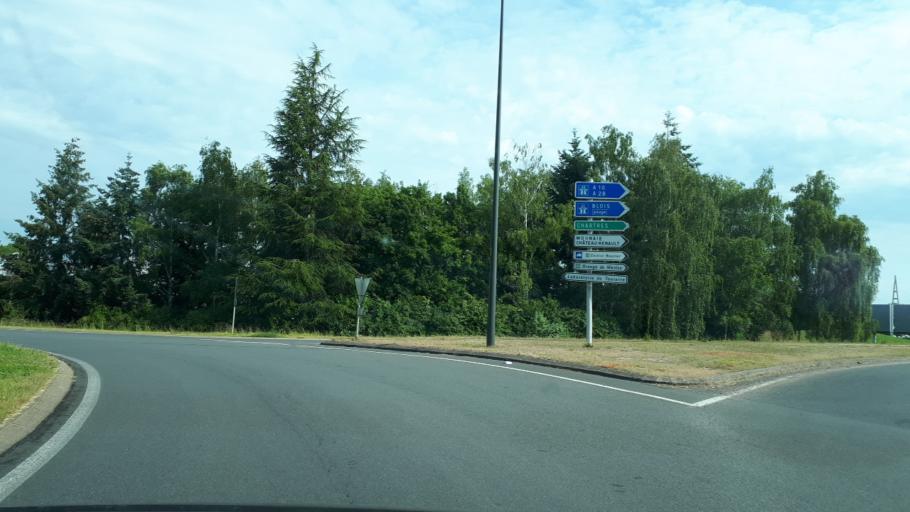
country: FR
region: Centre
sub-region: Departement d'Indre-et-Loire
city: Chanceaux-sur-Choisille
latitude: 47.4373
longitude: 0.7107
